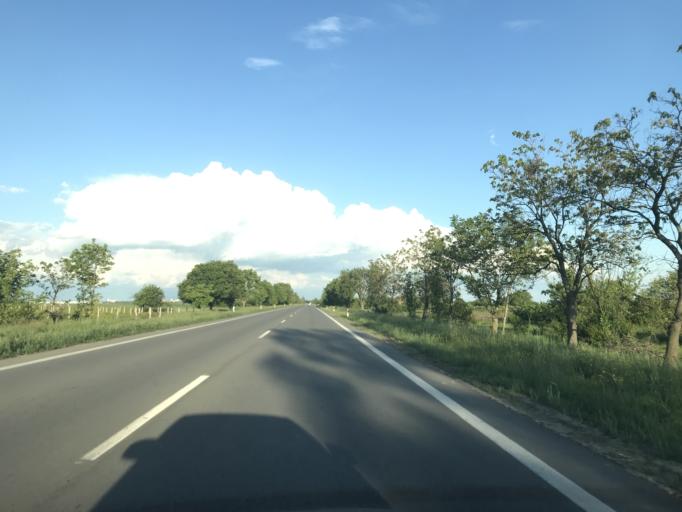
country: RS
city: Aradac
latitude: 45.3881
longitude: 20.3122
